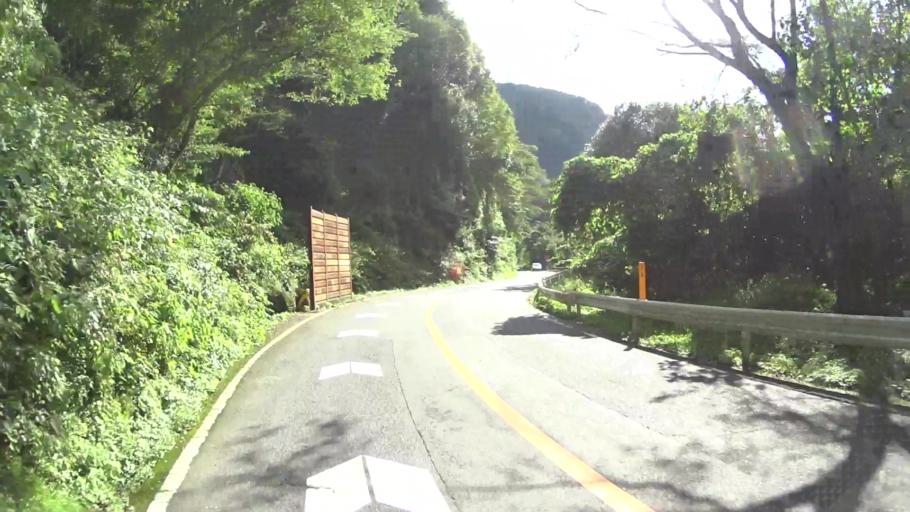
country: JP
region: Kyoto
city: Uji
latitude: 34.8930
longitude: 135.8685
